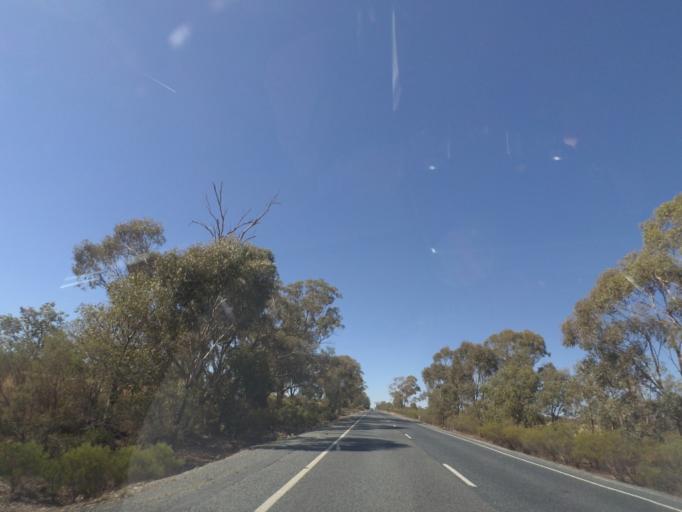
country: AU
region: New South Wales
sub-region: Bland
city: West Wyalong
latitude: -34.1596
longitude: 147.1170
